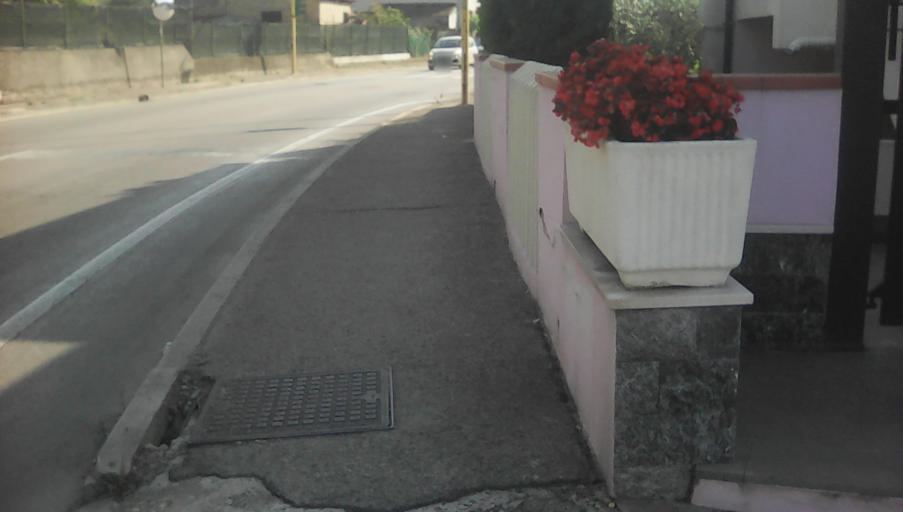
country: IT
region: Abruzzo
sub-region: Provincia di Pescara
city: Montesilvano Marina
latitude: 42.5062
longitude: 14.1444
